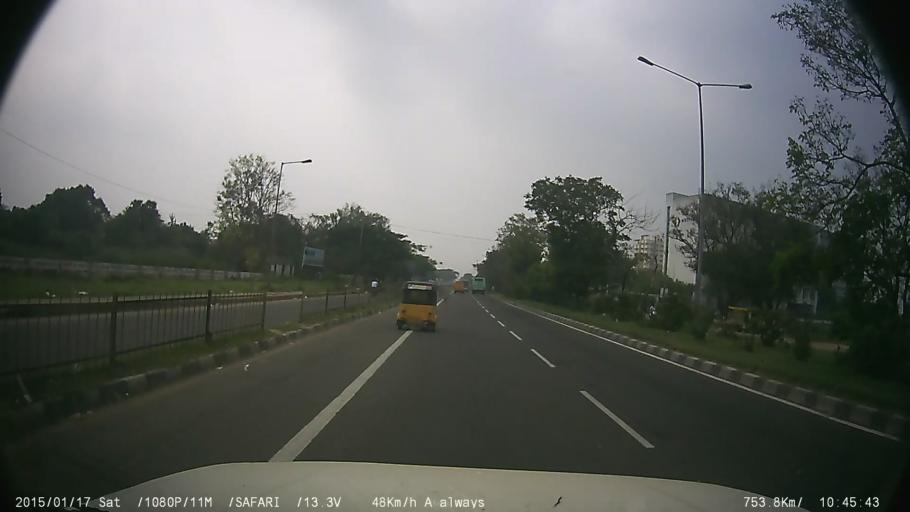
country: IN
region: Tamil Nadu
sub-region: Kancheepuram
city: Vandalur
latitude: 12.8760
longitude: 80.0790
